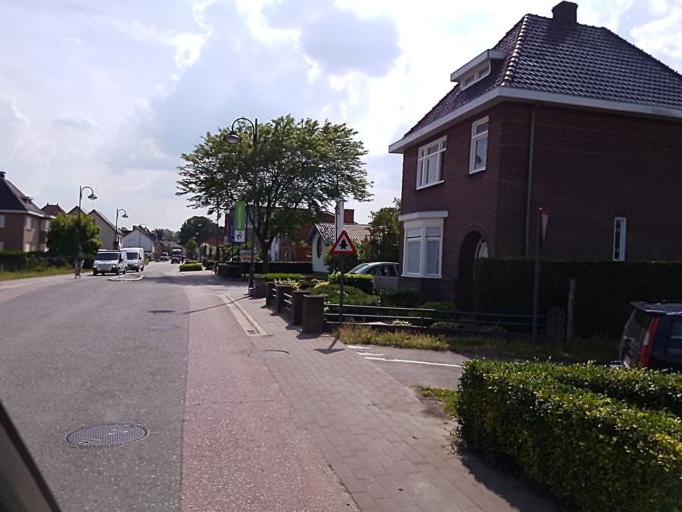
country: NL
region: North Brabant
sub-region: Gemeente Cranendonck
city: Cranendonck
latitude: 51.2552
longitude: 5.5534
